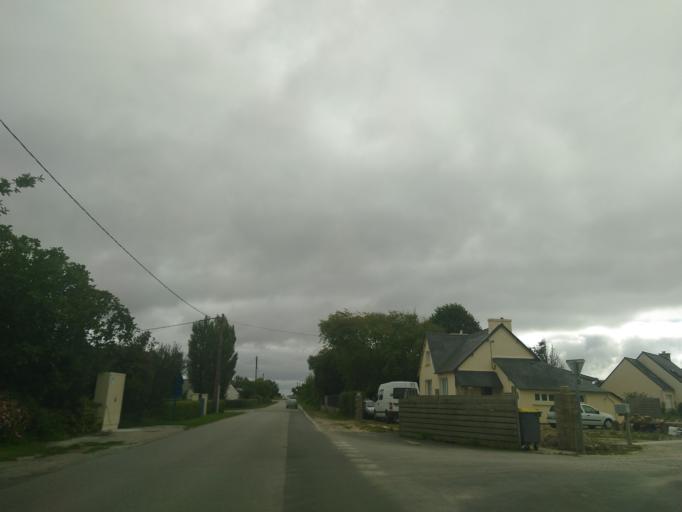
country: FR
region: Brittany
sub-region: Departement du Finistere
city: Plomodiern
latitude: 48.1685
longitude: -4.2744
